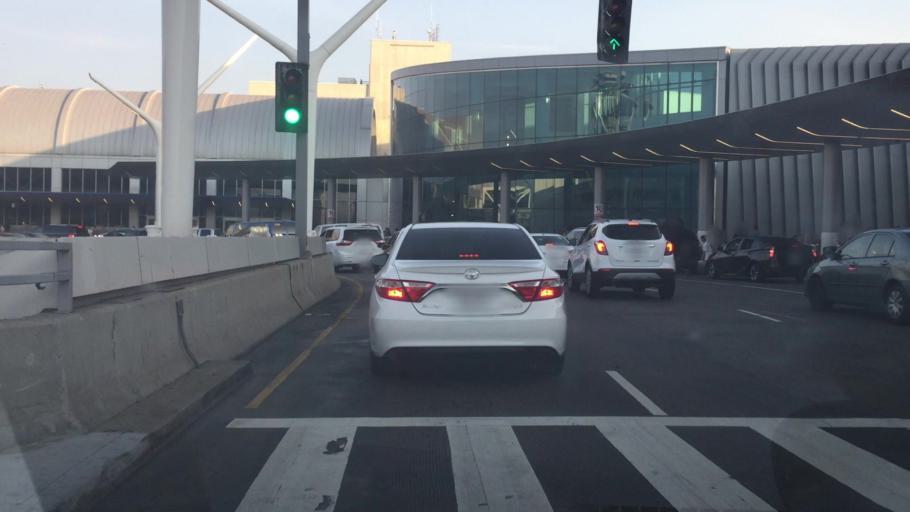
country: US
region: California
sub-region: Los Angeles County
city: El Segundo
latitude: 33.9430
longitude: -118.4080
